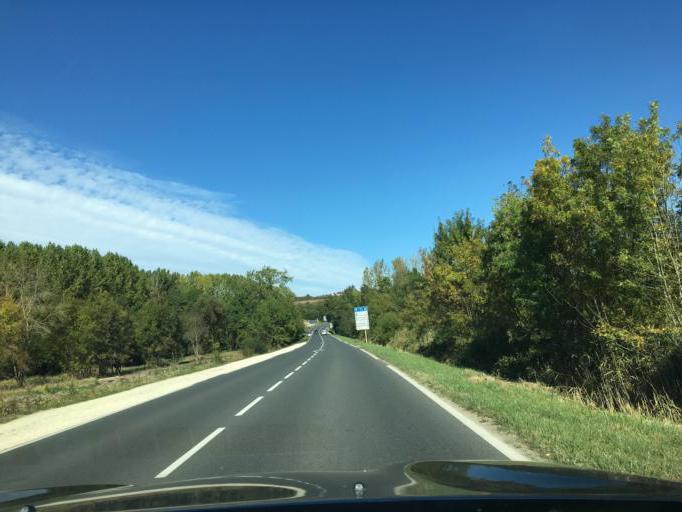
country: FR
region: Centre
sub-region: Departement d'Indre-et-Loire
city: Azay-le-Rideau
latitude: 47.2587
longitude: 0.4568
